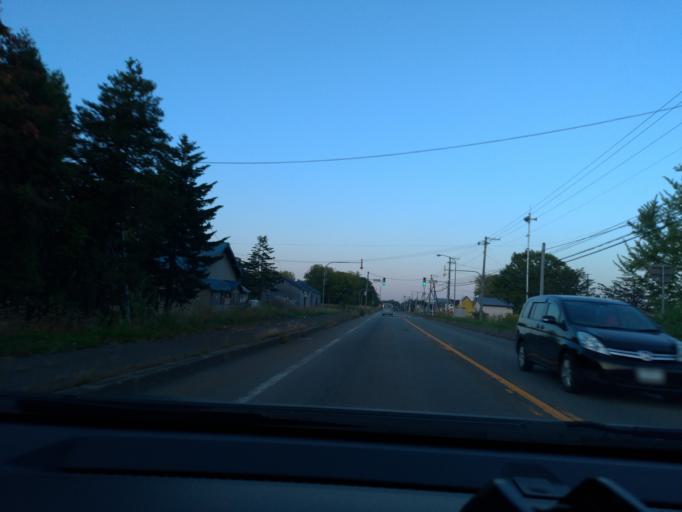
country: JP
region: Hokkaido
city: Tobetsu
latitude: 43.3217
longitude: 141.6127
